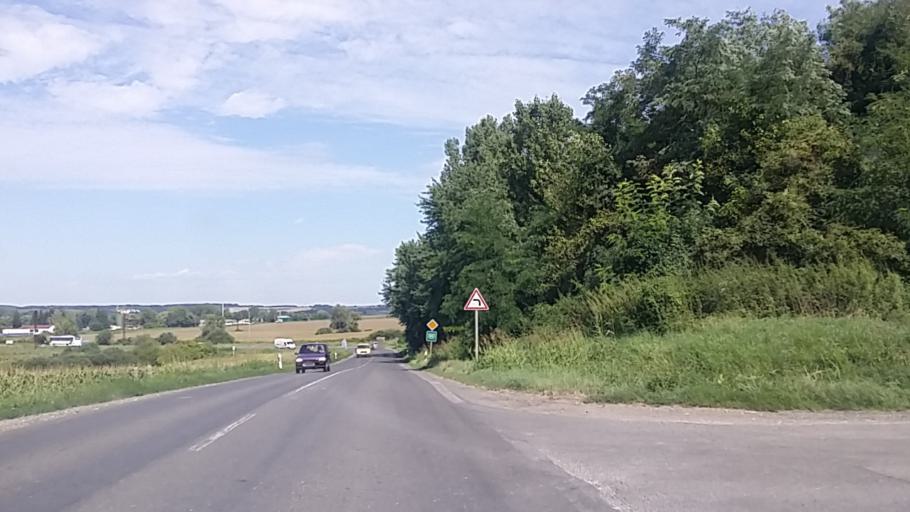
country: HU
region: Baranya
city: Sasd
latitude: 46.2485
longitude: 18.1199
